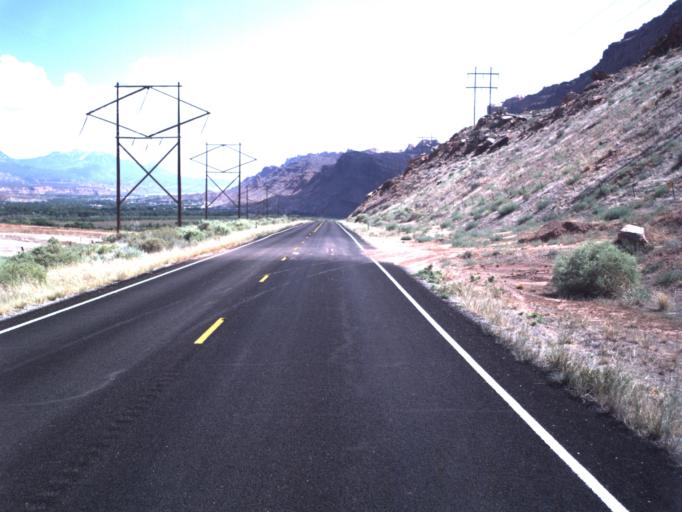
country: US
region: Utah
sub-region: Grand County
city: Moab
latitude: 38.5986
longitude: -109.6013
